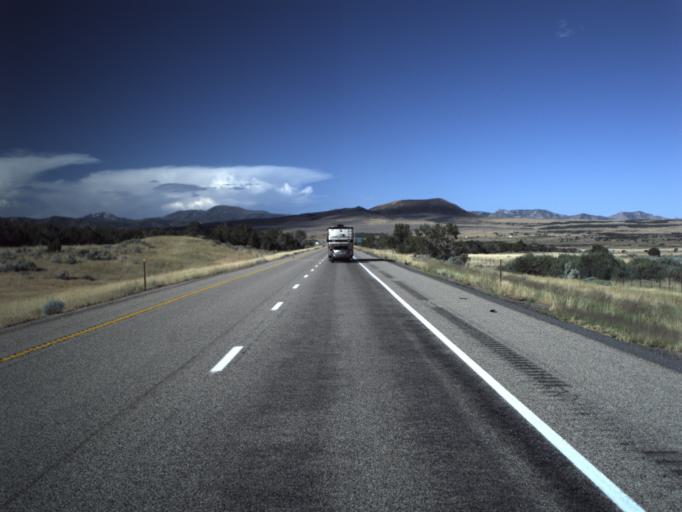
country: US
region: Utah
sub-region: Beaver County
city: Beaver
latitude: 38.5985
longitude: -112.5626
